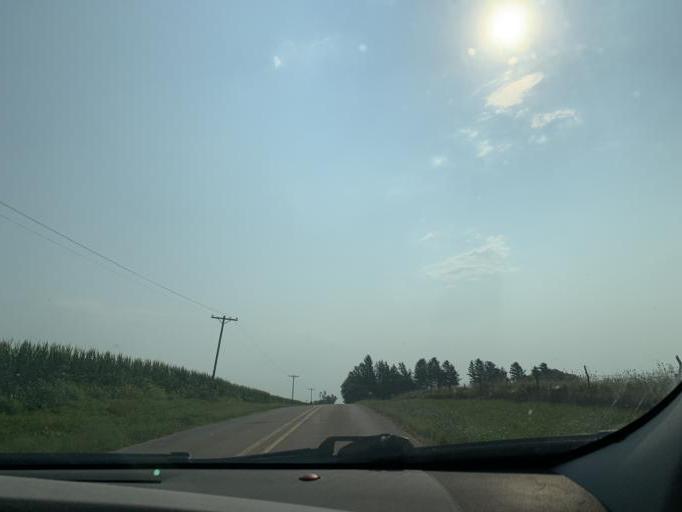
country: US
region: Illinois
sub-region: Whiteside County
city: Morrison
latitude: 41.8480
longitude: -89.8654
